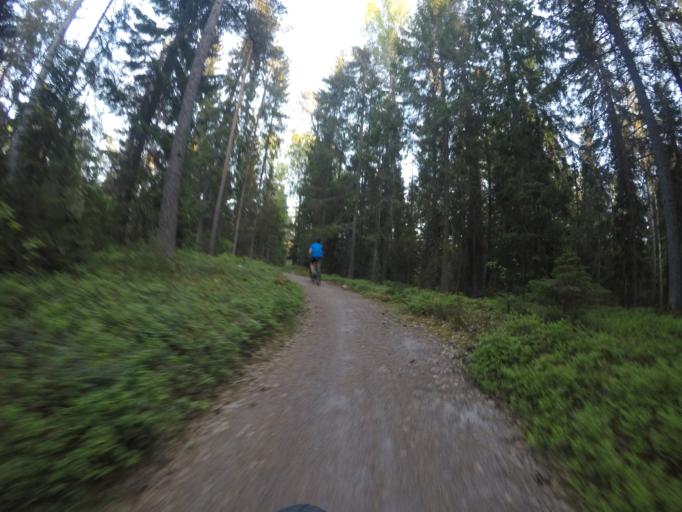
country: SE
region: Soedermanland
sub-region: Eskilstuna Kommun
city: Skogstorp
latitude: 59.3353
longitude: 16.5055
